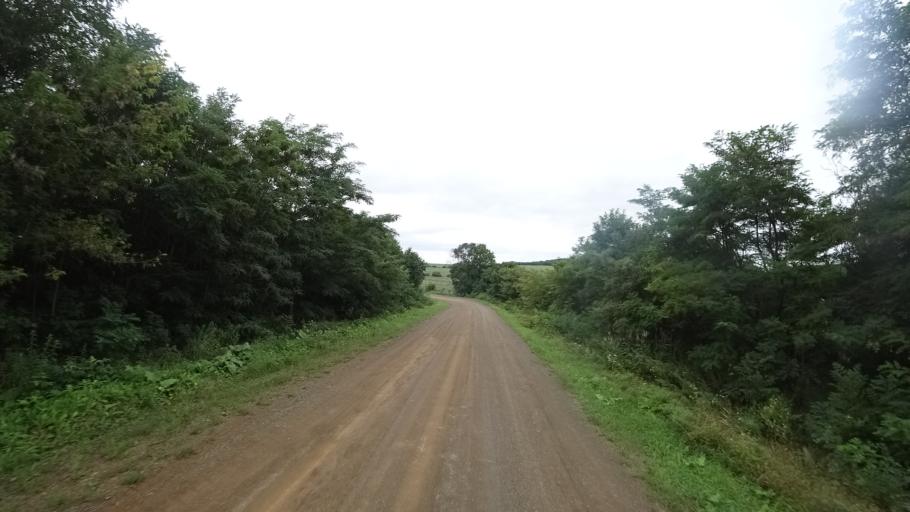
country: RU
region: Primorskiy
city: Chernigovka
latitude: 44.4537
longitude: 132.5839
